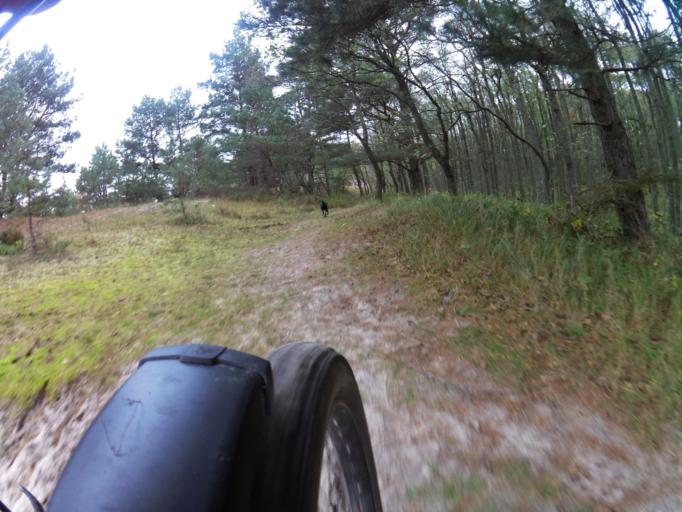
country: PL
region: Pomeranian Voivodeship
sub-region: Powiat leborski
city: Leba
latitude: 54.7745
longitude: 17.6655
